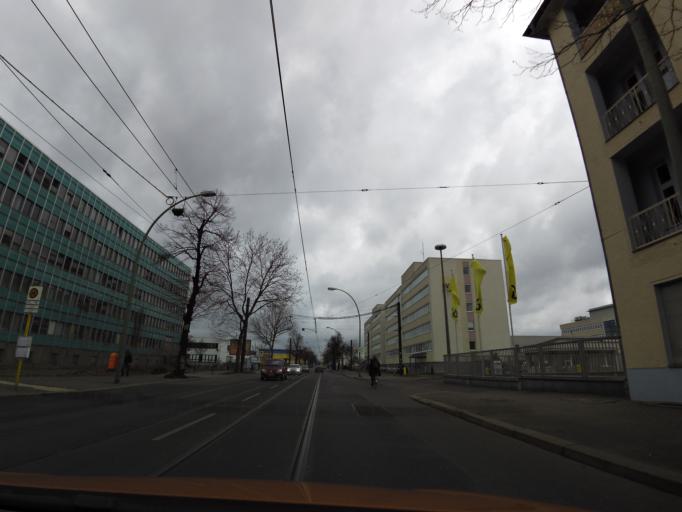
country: DE
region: Berlin
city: Lichtenberg
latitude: 52.5194
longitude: 13.4994
